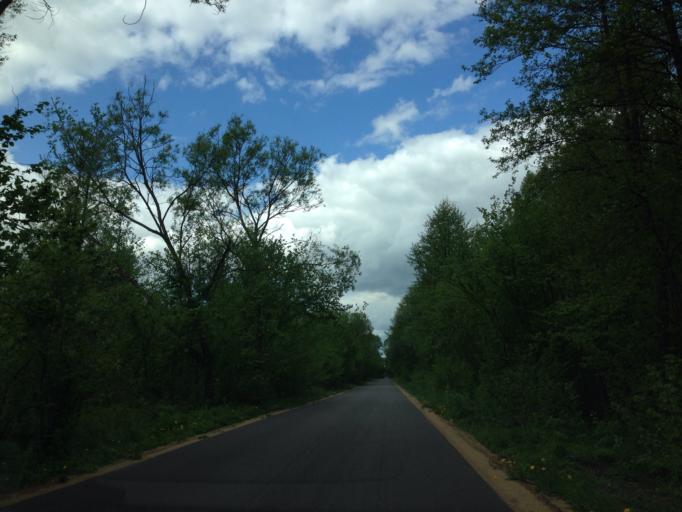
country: PL
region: Podlasie
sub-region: Powiat grajewski
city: Radzilow
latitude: 53.3240
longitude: 22.6011
